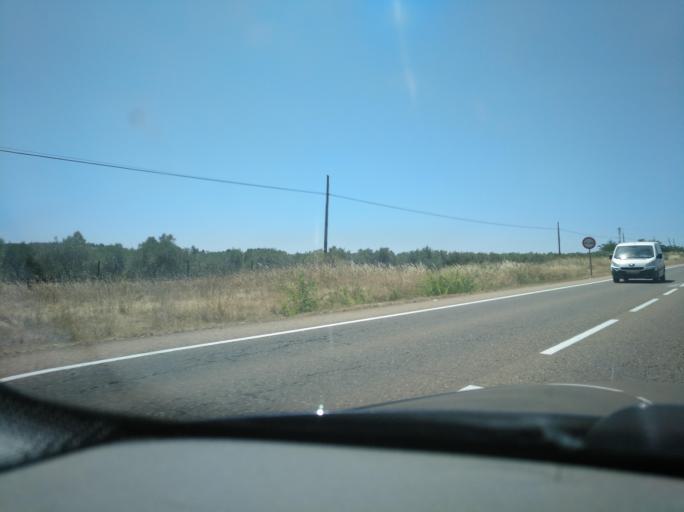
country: ES
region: Extremadura
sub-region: Provincia de Badajoz
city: Olivenza
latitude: 38.7339
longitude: -7.0692
